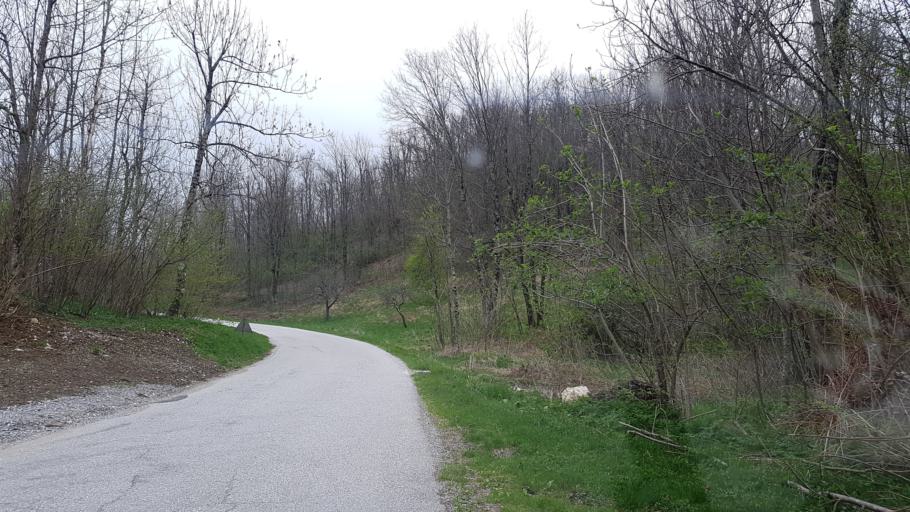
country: IT
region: Friuli Venezia Giulia
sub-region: Provincia di Udine
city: Pulfero
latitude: 46.2391
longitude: 13.4284
